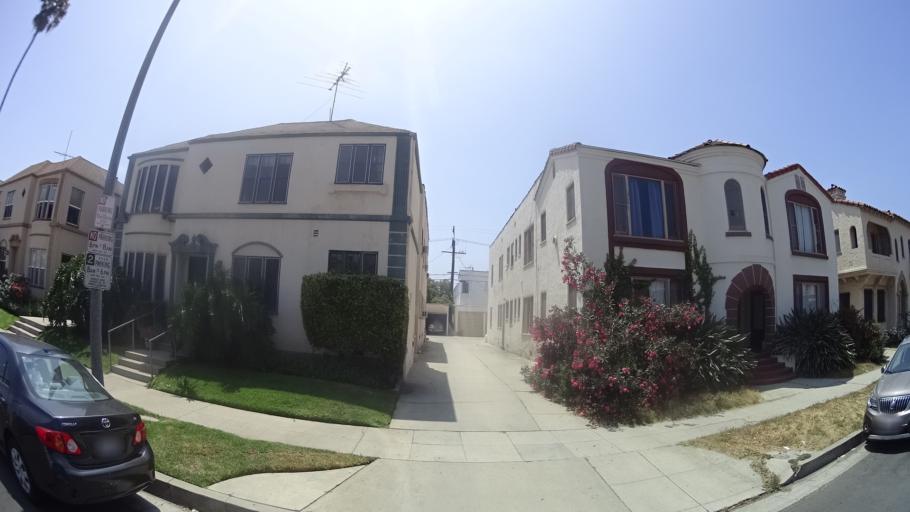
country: US
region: California
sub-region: Los Angeles County
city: West Hollywood
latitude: 34.0773
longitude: -118.3531
